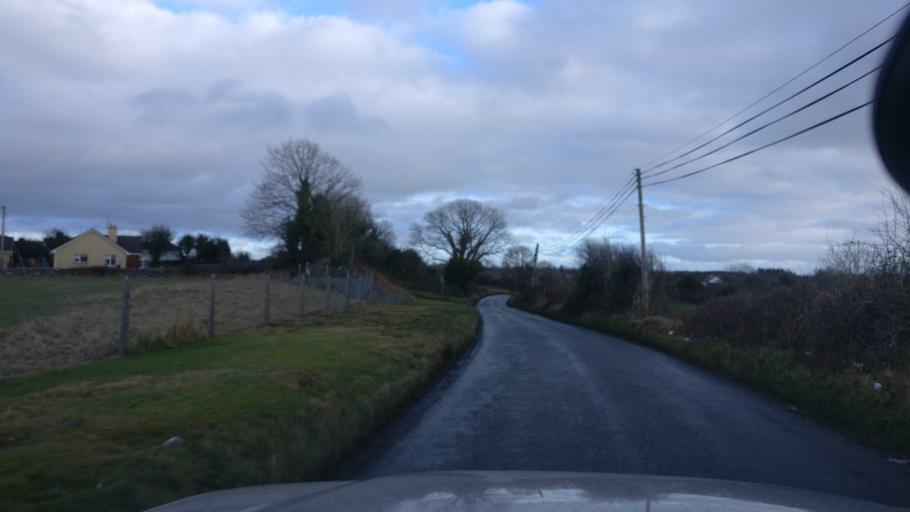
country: IE
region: Connaught
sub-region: County Galway
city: Athenry
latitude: 53.3004
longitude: -8.7233
